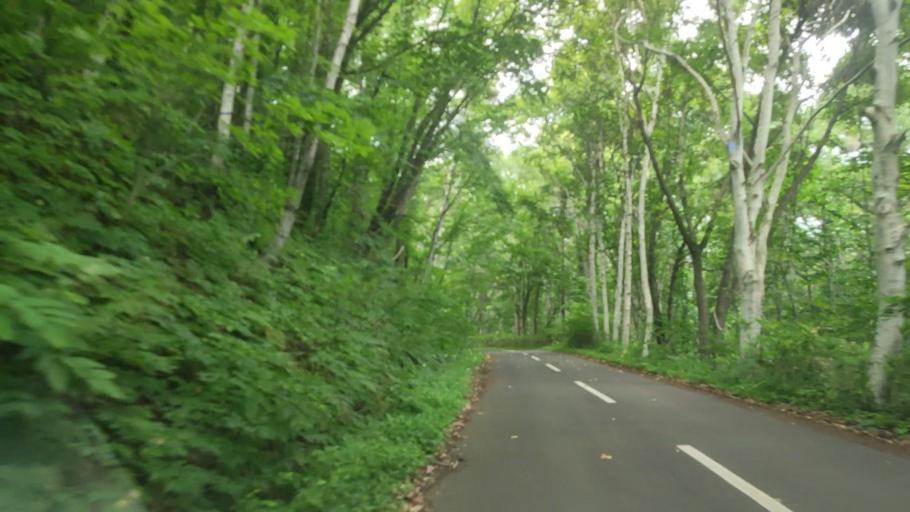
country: JP
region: Hokkaido
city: Otaru
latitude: 43.1949
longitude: 140.9846
